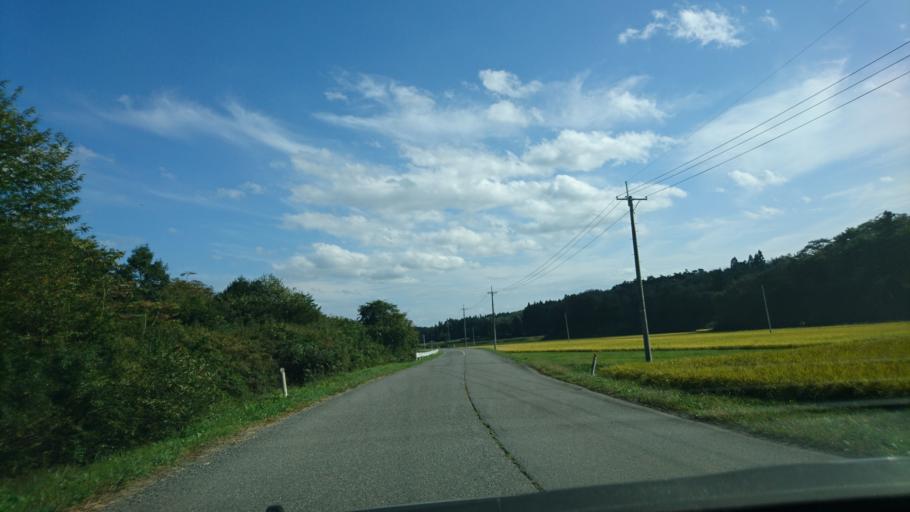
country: JP
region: Iwate
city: Ichinoseki
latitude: 38.8790
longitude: 141.0669
